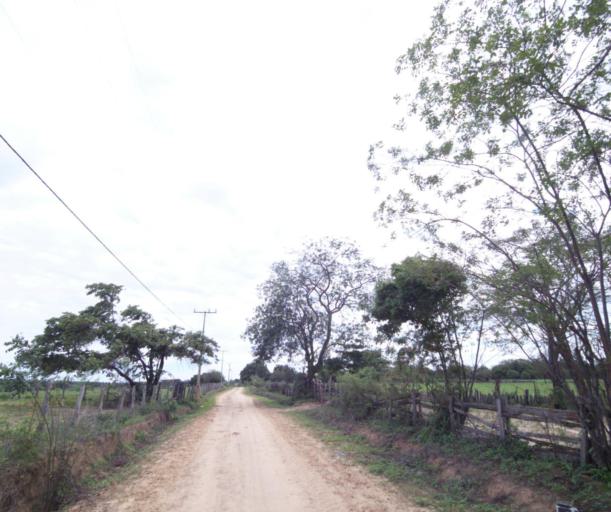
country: BR
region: Bahia
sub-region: Carinhanha
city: Carinhanha
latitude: -14.2508
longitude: -44.3519
